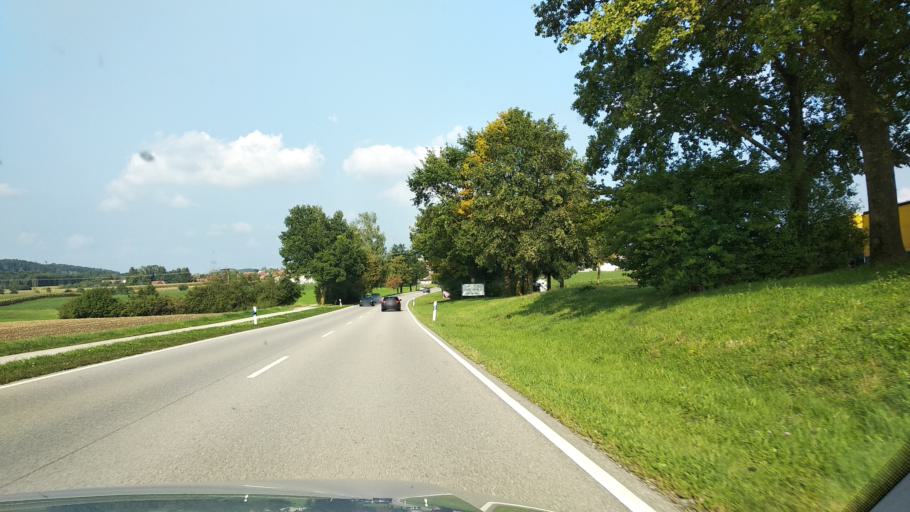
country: DE
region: Bavaria
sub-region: Upper Bavaria
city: Ebersberg
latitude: 48.0738
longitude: 11.9480
